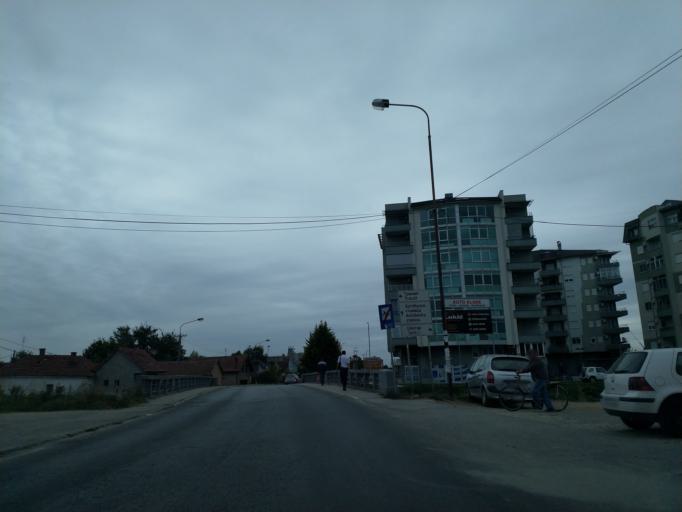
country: RS
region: Central Serbia
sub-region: Pomoravski Okrug
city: Jagodina
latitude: 43.9866
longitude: 21.2480
